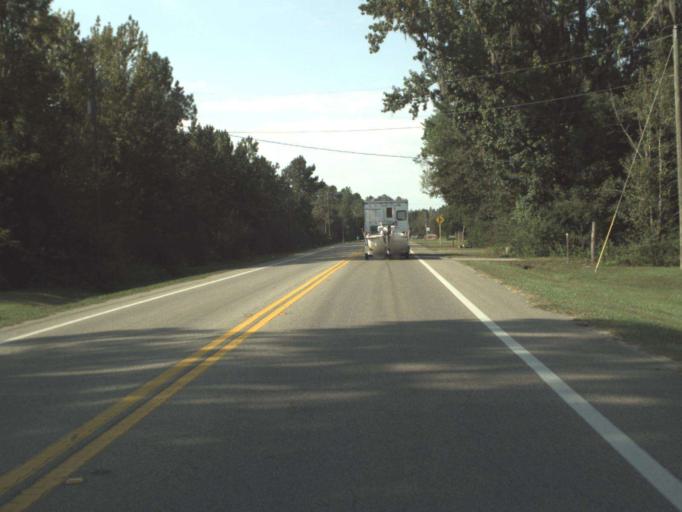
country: US
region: Florida
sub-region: Gulf County
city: Wewahitchka
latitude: 30.1366
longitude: -85.2089
